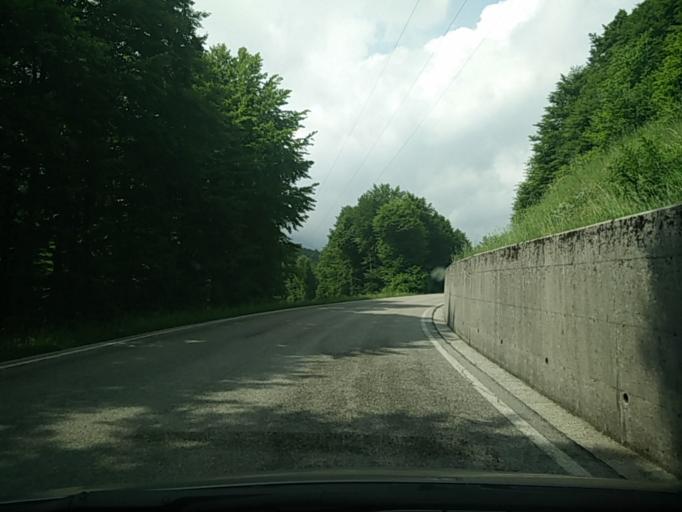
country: IT
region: Friuli Venezia Giulia
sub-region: Provincia di Pordenone
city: Budoia
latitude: 46.0981
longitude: 12.5281
